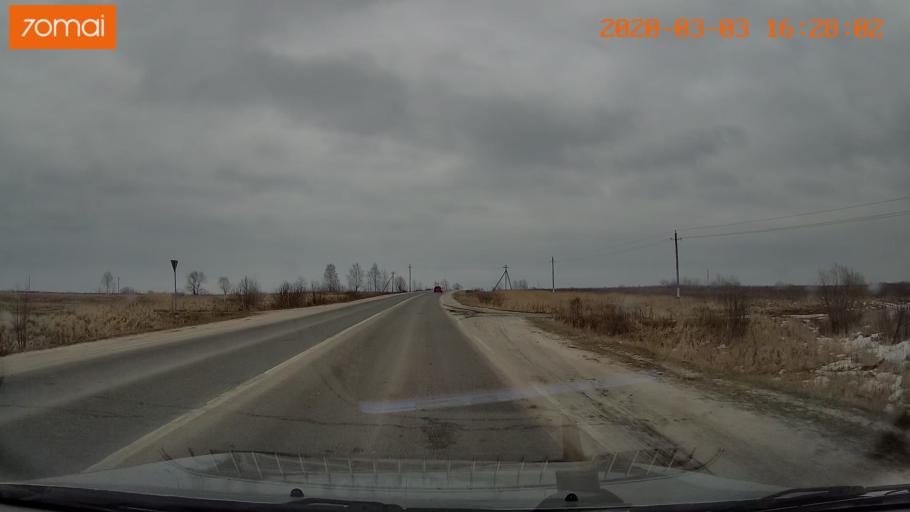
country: RU
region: Moskovskaya
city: Konobeyevo
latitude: 55.4374
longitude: 38.6781
